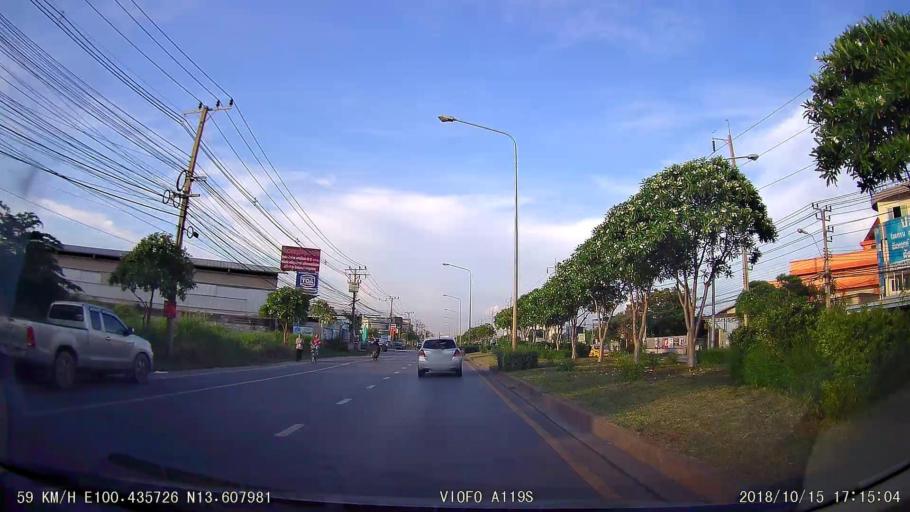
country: TH
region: Bangkok
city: Bang Khun Thian
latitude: 13.6082
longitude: 100.4358
